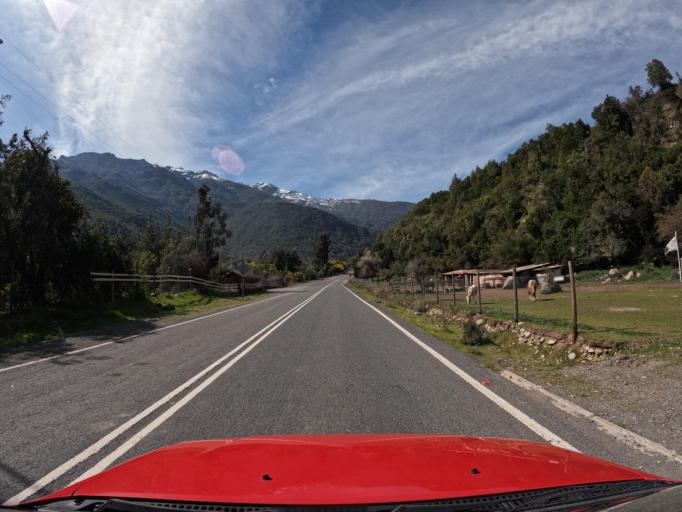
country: CL
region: O'Higgins
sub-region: Provincia de Colchagua
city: Chimbarongo
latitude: -35.0002
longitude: -70.8227
